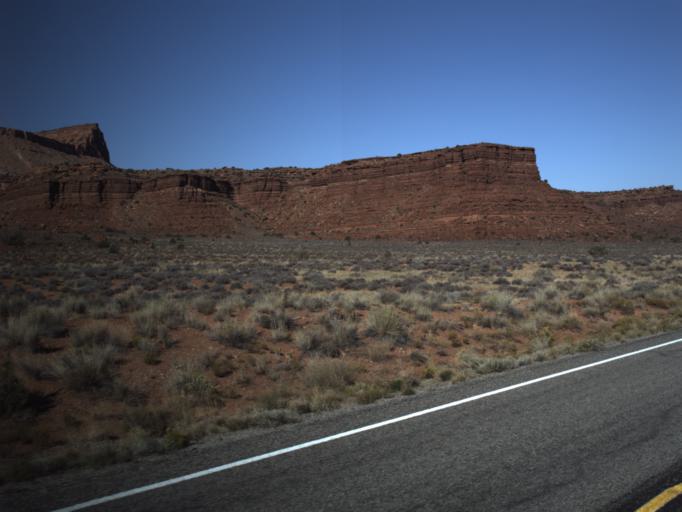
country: US
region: Utah
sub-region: San Juan County
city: Blanding
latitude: 37.7901
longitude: -110.2986
